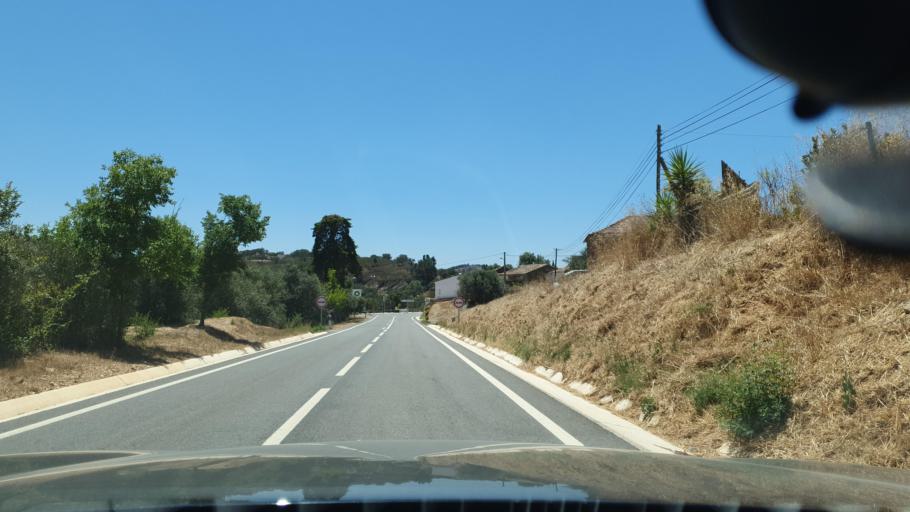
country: PT
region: Beja
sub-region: Odemira
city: Odemira
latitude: 37.5146
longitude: -8.4763
